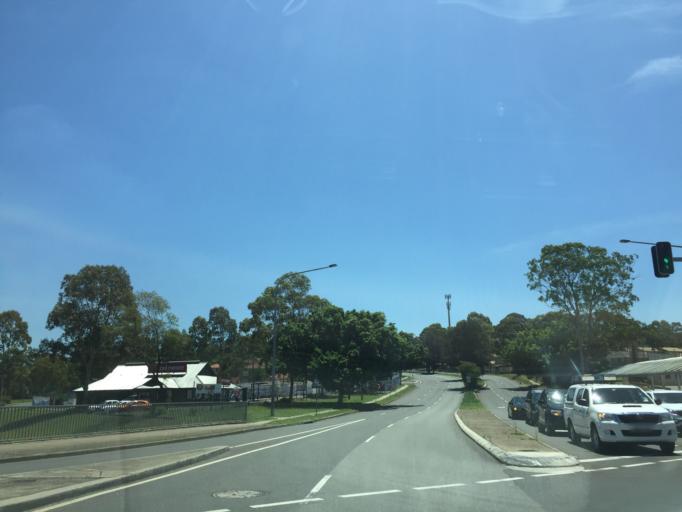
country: AU
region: New South Wales
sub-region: Blacktown
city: Blacktown
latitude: -33.7797
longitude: 150.9204
